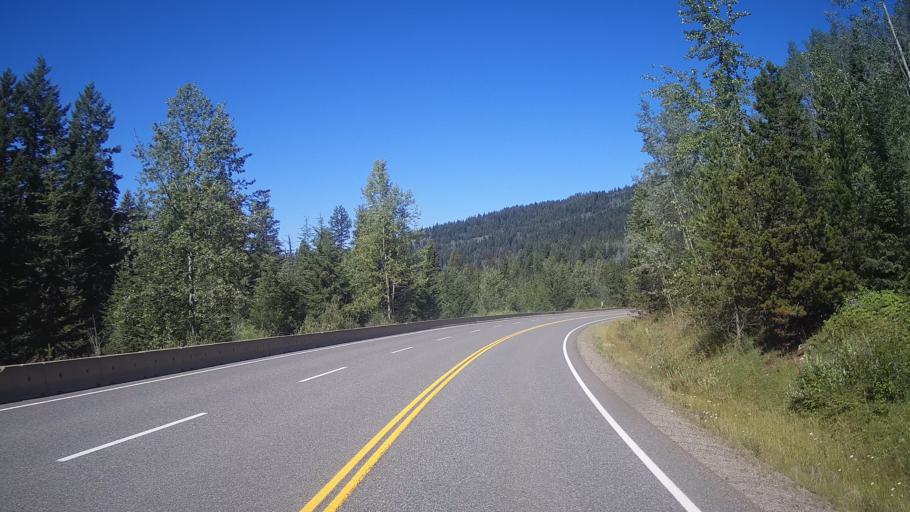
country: CA
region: British Columbia
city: Kamloops
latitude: 51.4761
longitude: -120.4784
